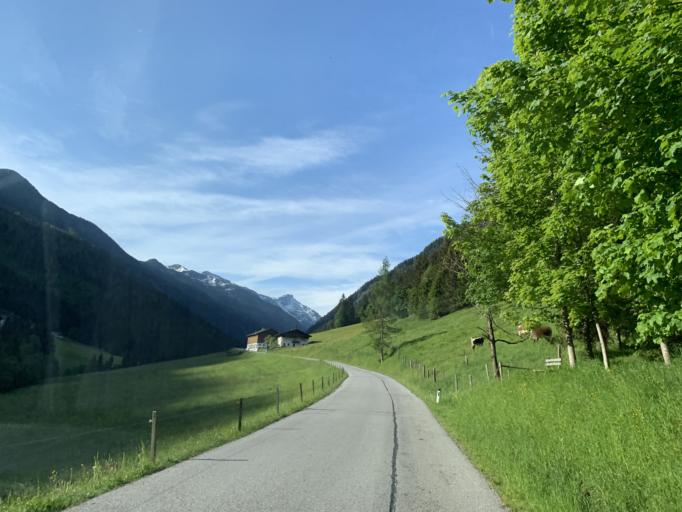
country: AT
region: Styria
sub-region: Politischer Bezirk Liezen
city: Schladming
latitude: 47.3689
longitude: 13.6148
